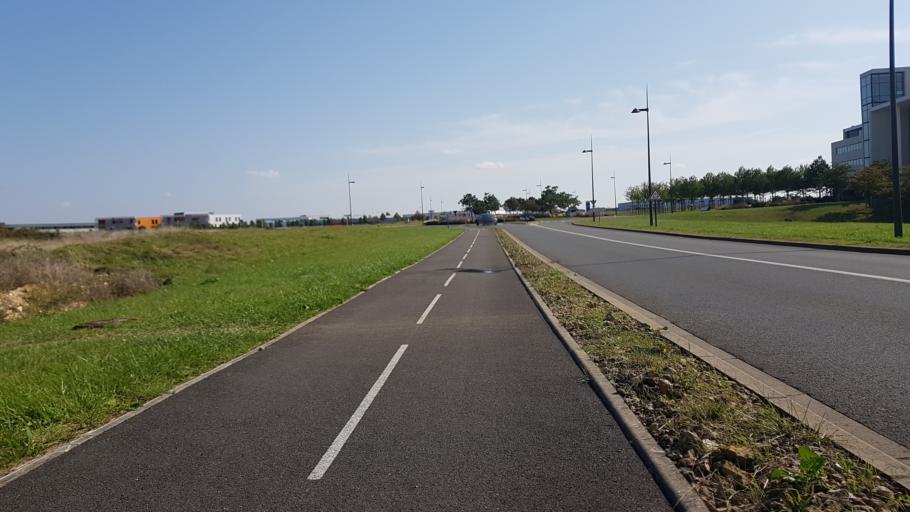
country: FR
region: Poitou-Charentes
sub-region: Departement de la Vienne
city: Chasseneuil-du-Poitou
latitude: 46.6560
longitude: 0.3590
